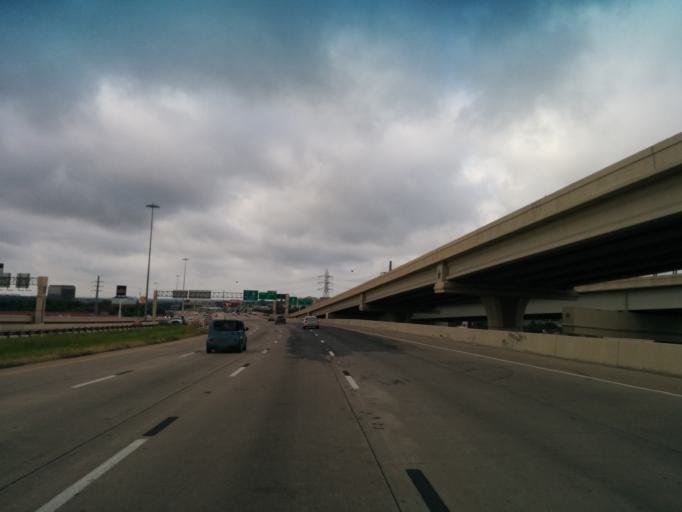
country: US
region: Texas
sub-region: Bexar County
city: Balcones Heights
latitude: 29.4971
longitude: -98.5482
